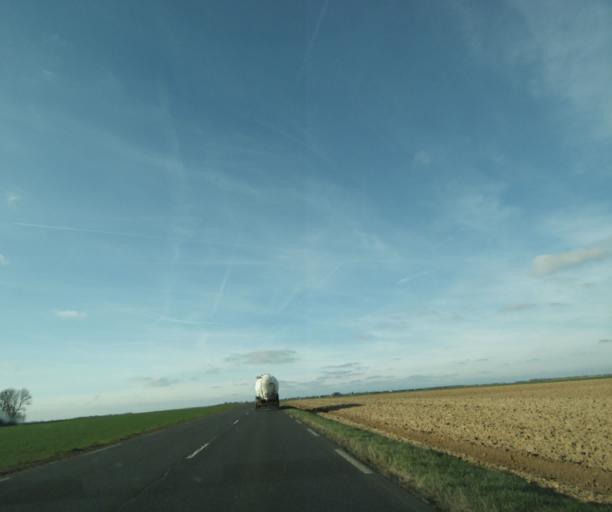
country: FR
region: Ile-de-France
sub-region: Departement des Yvelines
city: Ablis
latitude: 48.4962
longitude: 1.8424
